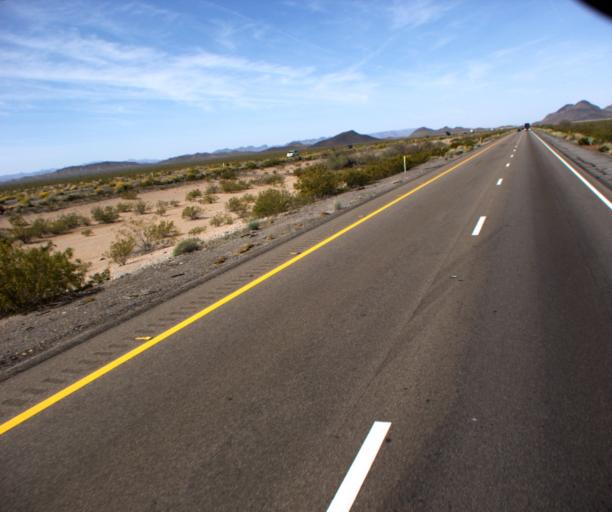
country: US
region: Arizona
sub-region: La Paz County
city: Salome
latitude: 33.6011
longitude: -113.5647
